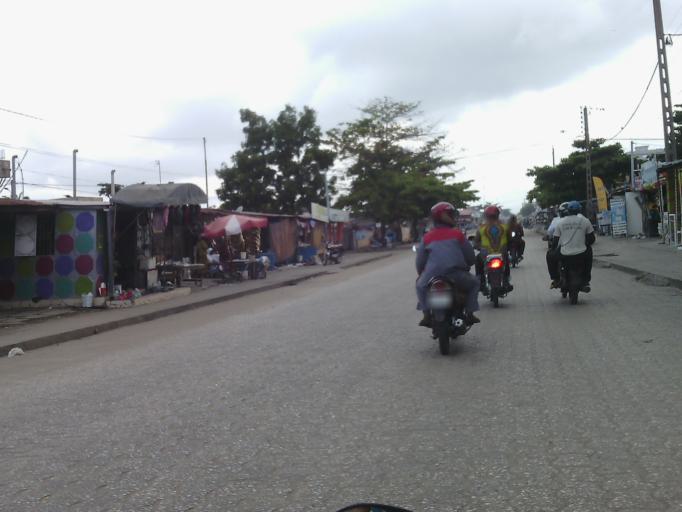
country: BJ
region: Littoral
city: Cotonou
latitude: 6.3715
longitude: 2.4164
